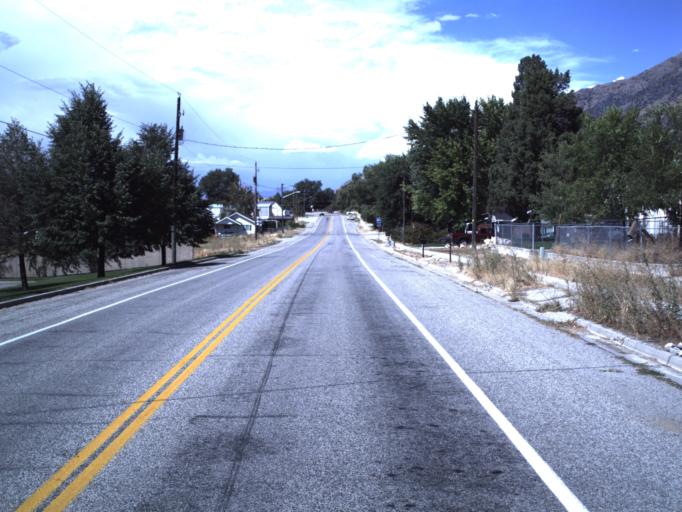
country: US
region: Utah
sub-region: Box Elder County
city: Honeyville
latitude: 41.6373
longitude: -112.0796
